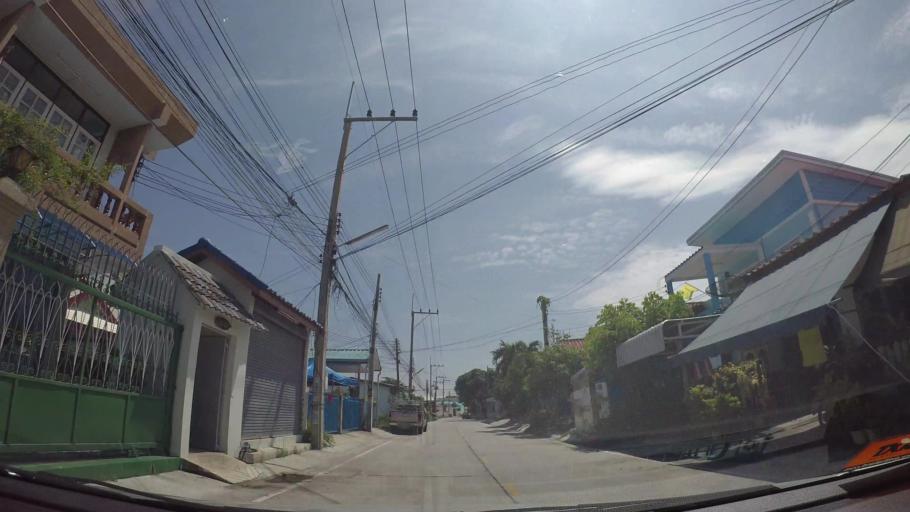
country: TH
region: Chon Buri
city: Chon Buri
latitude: 13.3187
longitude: 100.9569
